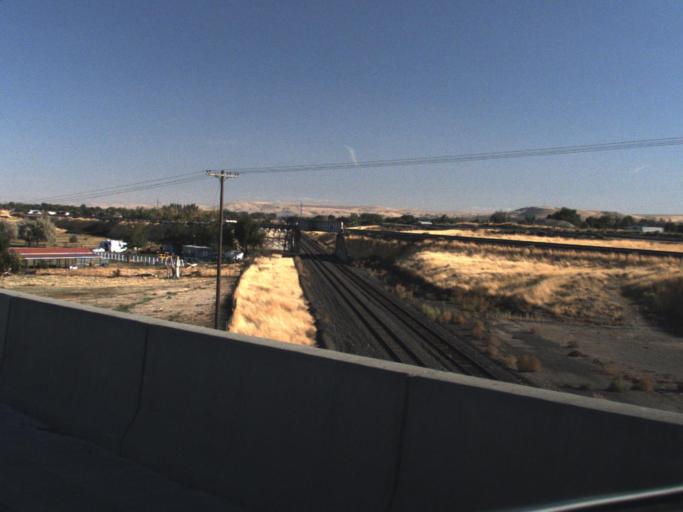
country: US
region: Washington
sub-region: Franklin County
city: Pasco
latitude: 46.1986
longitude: -119.0912
